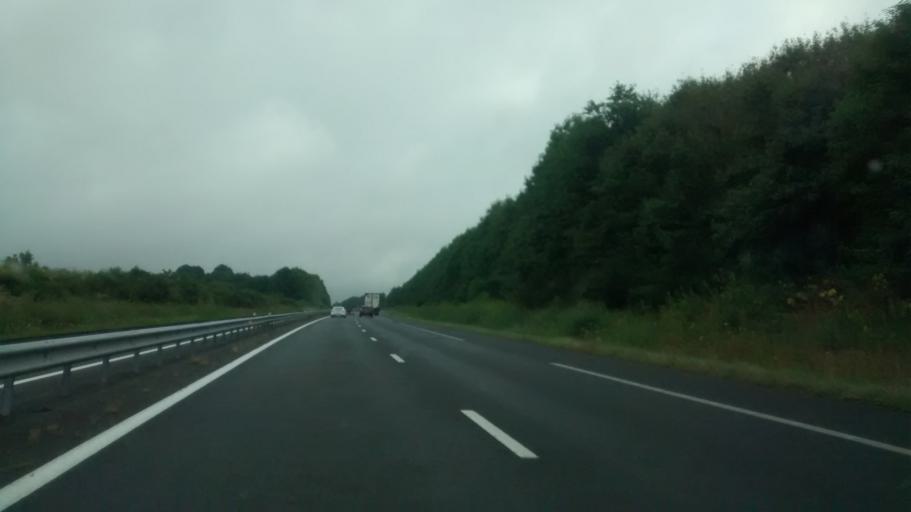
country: FR
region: Brittany
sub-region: Departement d'Ille-et-Vilaine
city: Saint-Etienne-en-Cogles
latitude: 48.4119
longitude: -1.3122
